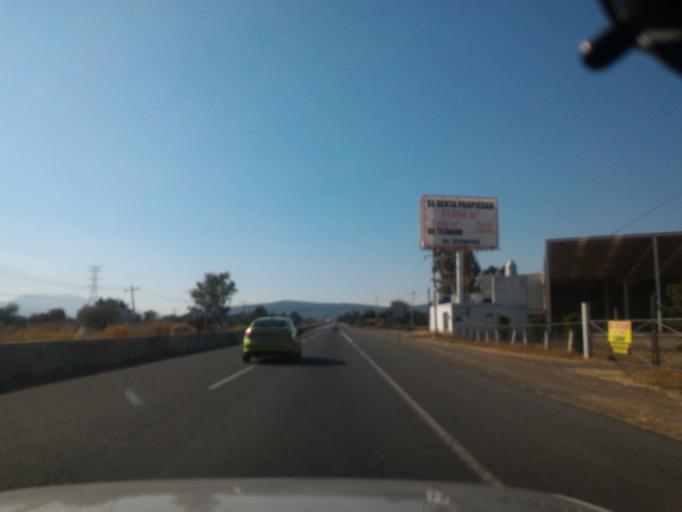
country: MX
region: Jalisco
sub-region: Ixtlahuacan de los Membrillos
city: Valle de los Girasoles [Fraccionamiento]
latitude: 20.4114
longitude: -103.2145
